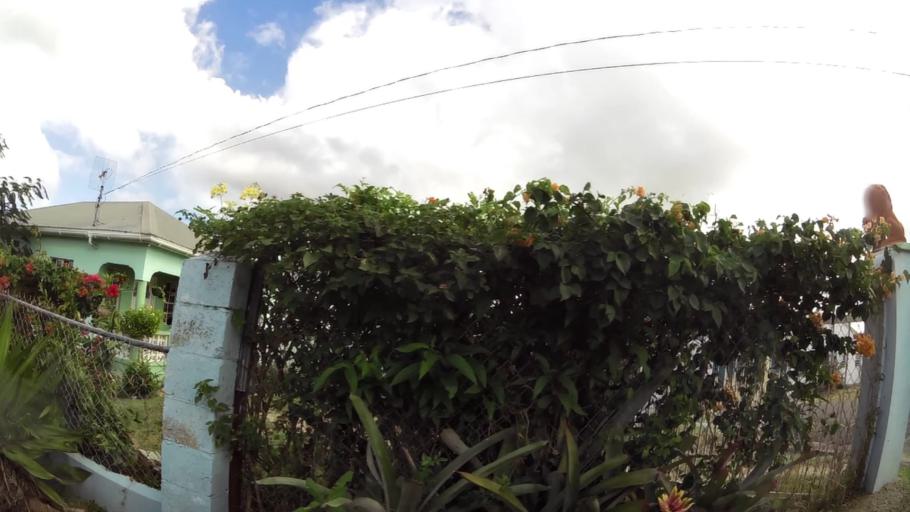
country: AG
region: Saint John
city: Saint John's
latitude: 17.1097
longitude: -61.8565
